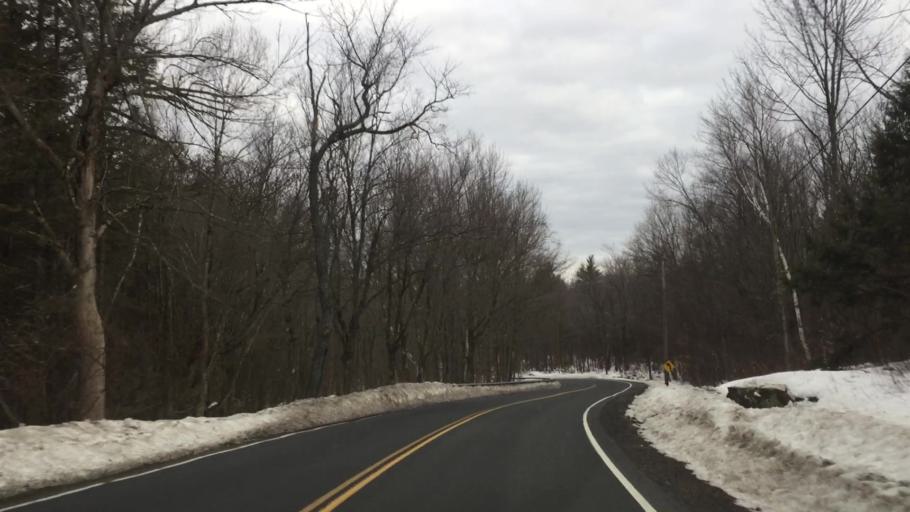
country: US
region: Massachusetts
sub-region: Berkshire County
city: Hinsdale
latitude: 42.4125
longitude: -73.0642
